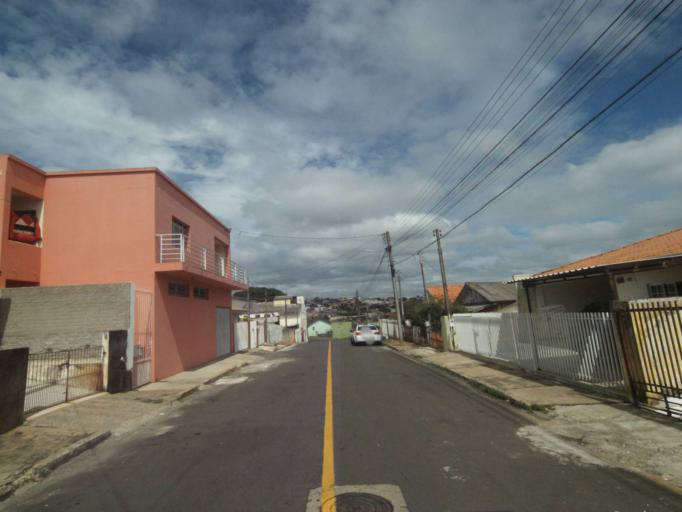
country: BR
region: Parana
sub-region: Telemaco Borba
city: Telemaco Borba
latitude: -24.3279
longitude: -50.6292
